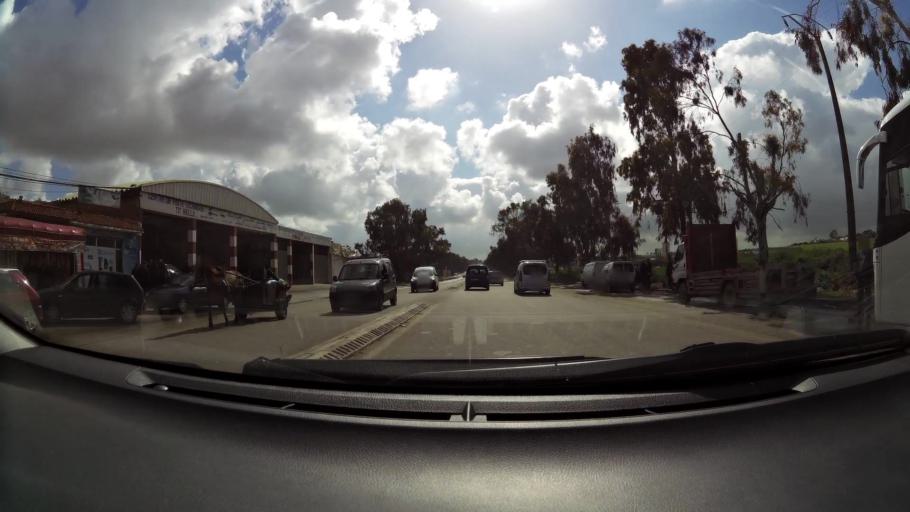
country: MA
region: Grand Casablanca
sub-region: Mediouna
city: Tit Mellil
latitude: 33.5674
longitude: -7.5104
